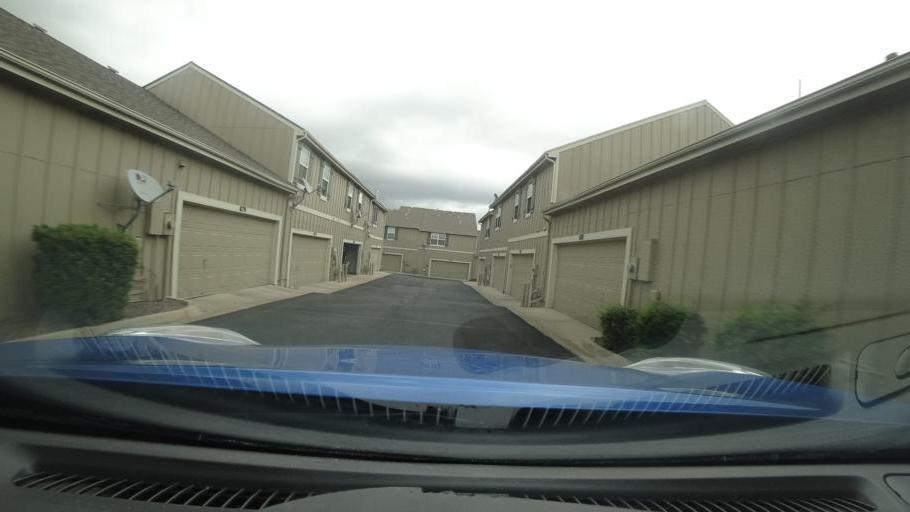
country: US
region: Colorado
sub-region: Adams County
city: Aurora
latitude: 39.7002
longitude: -104.8110
